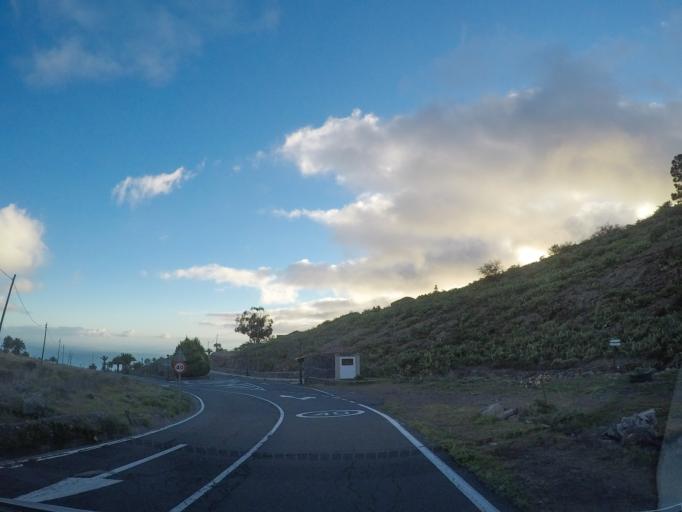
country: ES
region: Canary Islands
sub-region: Provincia de Santa Cruz de Tenerife
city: Alajero
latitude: 28.0699
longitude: -17.2388
